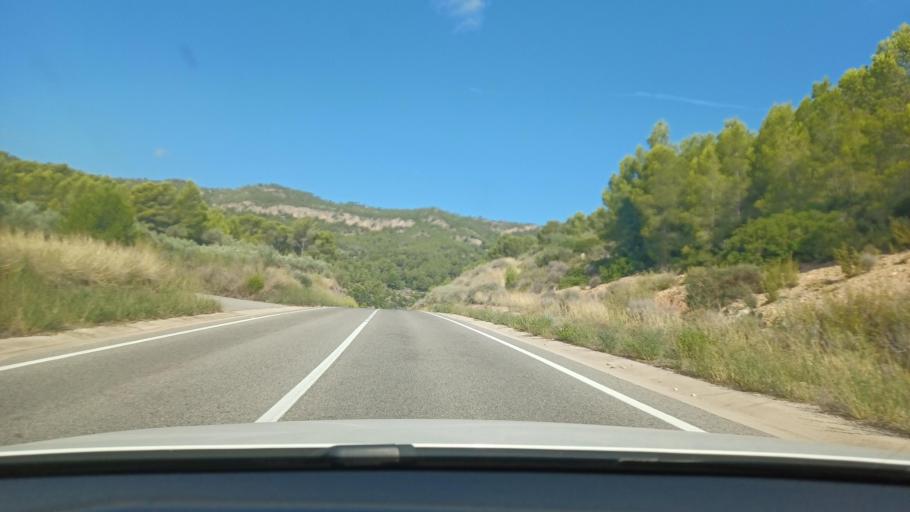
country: ES
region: Catalonia
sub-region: Provincia de Tarragona
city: Tivenys
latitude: 40.9407
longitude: 0.4649
